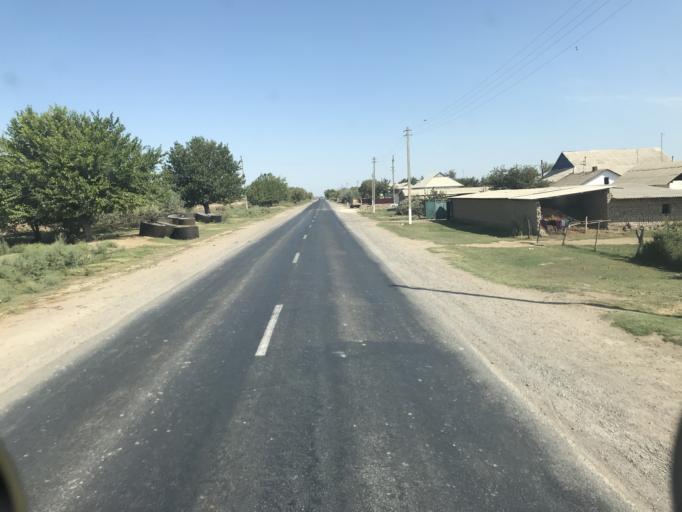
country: KZ
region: Ongtustik Qazaqstan
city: Ilyich
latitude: 40.7625
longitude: 68.5371
